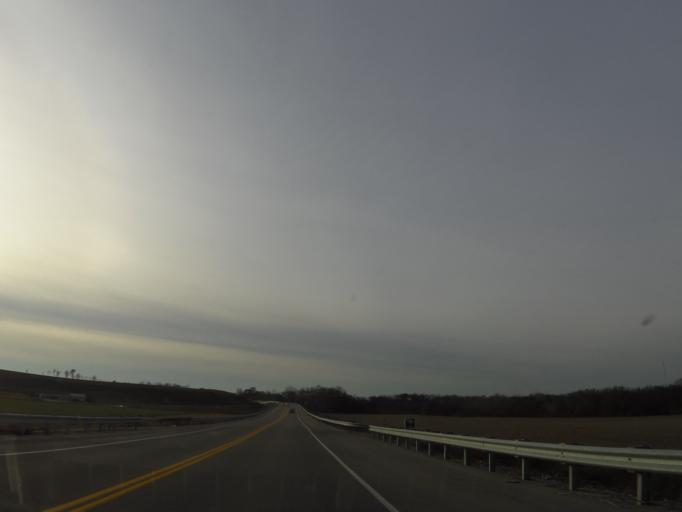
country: US
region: Kentucky
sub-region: Harrison County
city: Cynthiana
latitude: 38.3991
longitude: -84.3027
